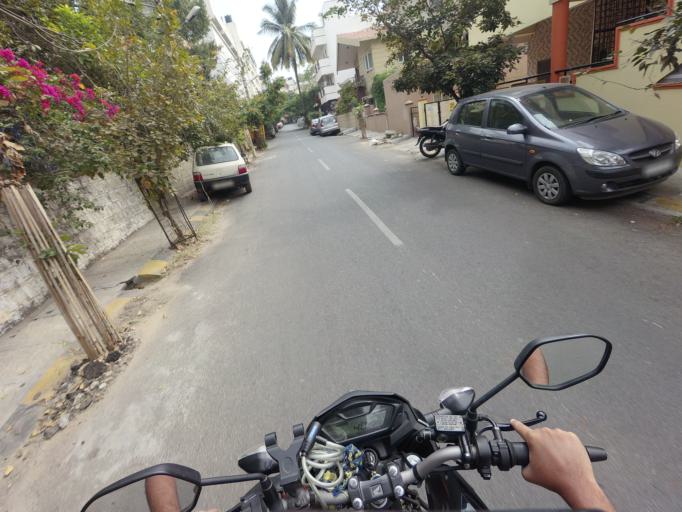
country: IN
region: Karnataka
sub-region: Bangalore Urban
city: Bangalore
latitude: 12.9702
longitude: 77.5353
